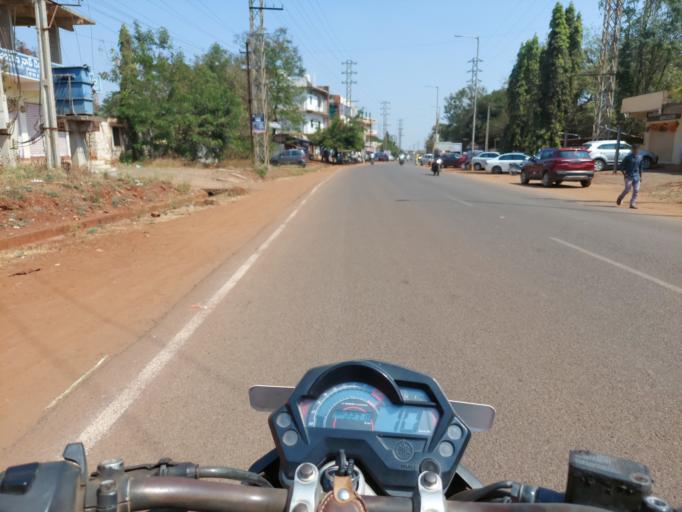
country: IN
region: Telangana
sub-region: Rangareddi
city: Vikarabad
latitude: 17.3337
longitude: 77.8997
